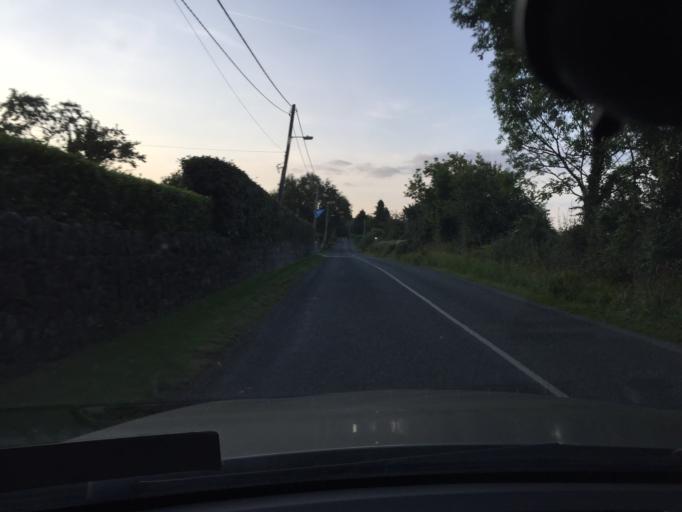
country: IE
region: Leinster
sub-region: Wicklow
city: Enniskerry
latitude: 53.1941
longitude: -6.1904
